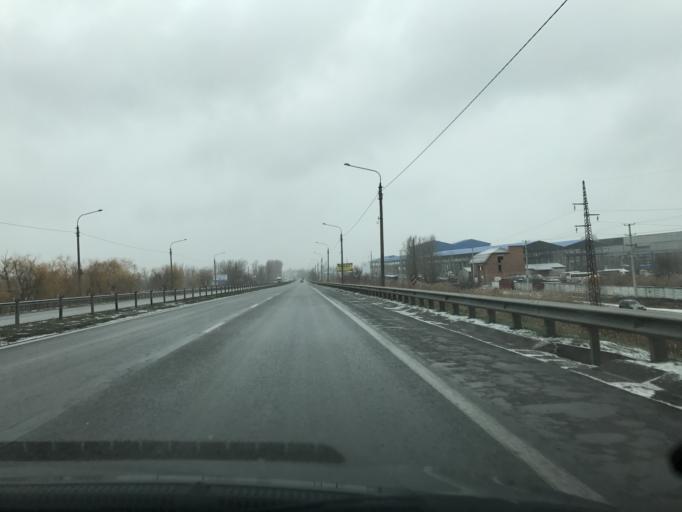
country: RU
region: Rostov
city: Bataysk
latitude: 47.1183
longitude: 39.7701
